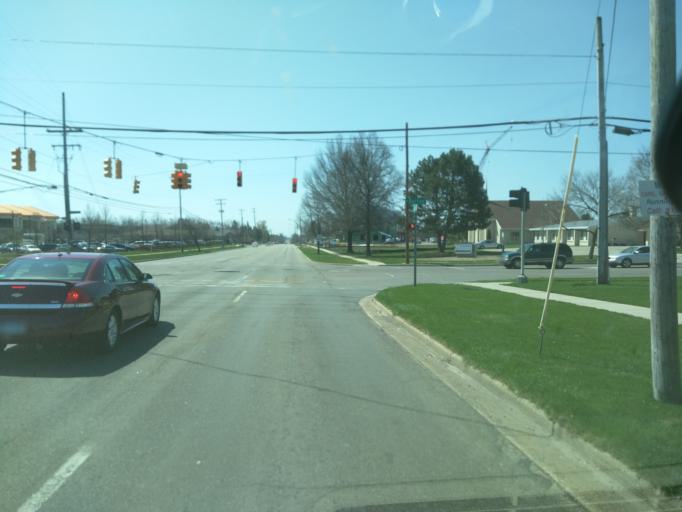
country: US
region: Michigan
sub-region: Kent County
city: East Grand Rapids
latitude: 42.9273
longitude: -85.5697
